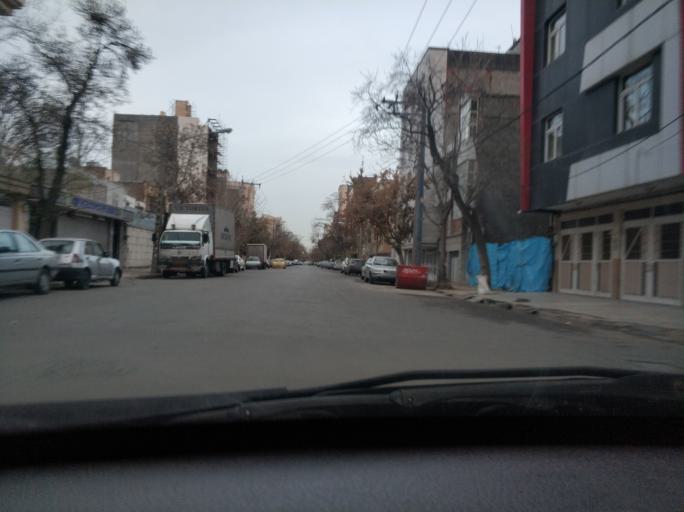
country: IR
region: Razavi Khorasan
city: Mashhad
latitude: 36.2747
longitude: 59.5960
